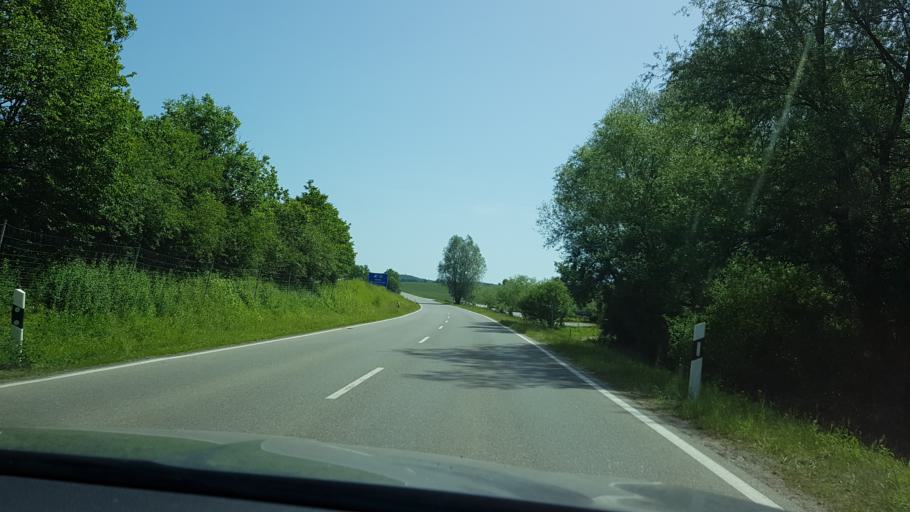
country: DE
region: Bavaria
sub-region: Upper Bavaria
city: Inning am Ammersee
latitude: 48.0788
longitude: 11.1349
